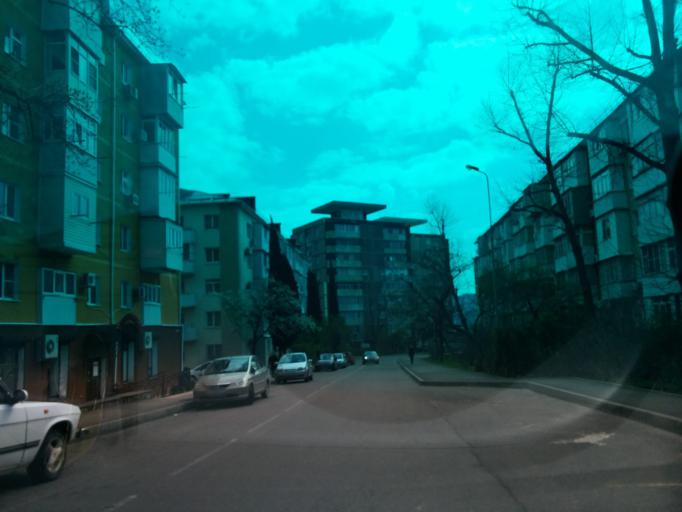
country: RU
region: Krasnodarskiy
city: Tuapse
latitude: 44.1055
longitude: 39.0837
